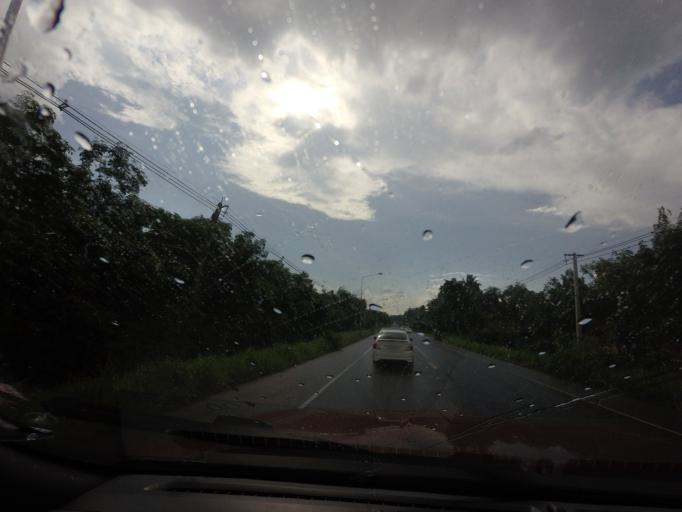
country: TH
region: Pattani
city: Mae Lan
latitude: 6.6589
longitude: 101.1698
